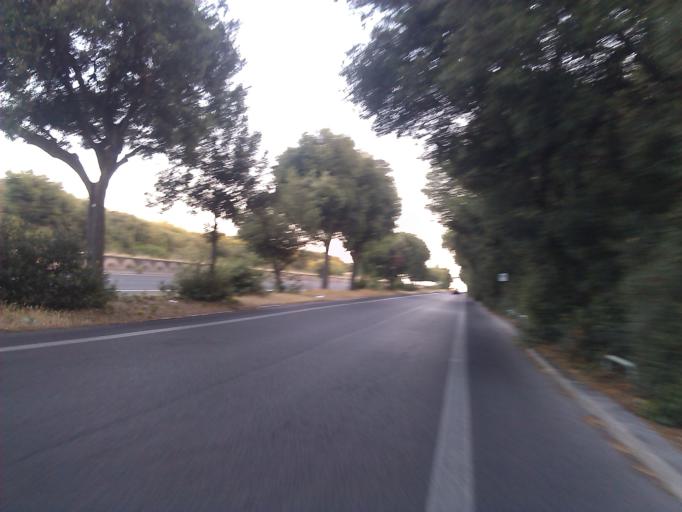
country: IT
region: Latium
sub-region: Citta metropolitana di Roma Capitale
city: Acilia-Castel Fusano-Ostia Antica
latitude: 41.7185
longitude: 12.3220
